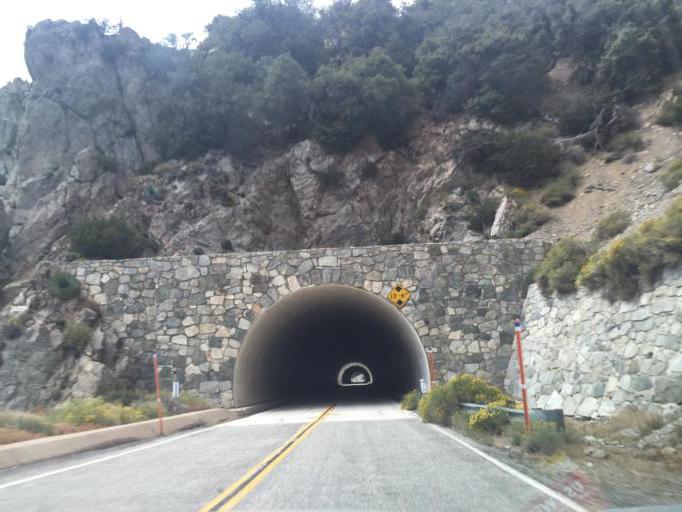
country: US
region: California
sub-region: Los Angeles County
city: Littlerock
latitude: 34.3606
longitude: -117.8607
